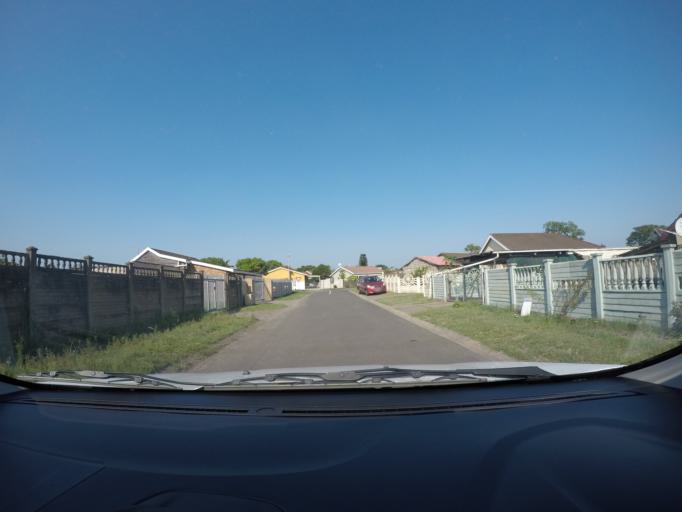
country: ZA
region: KwaZulu-Natal
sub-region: uThungulu District Municipality
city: Richards Bay
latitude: -28.7158
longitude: 32.0329
